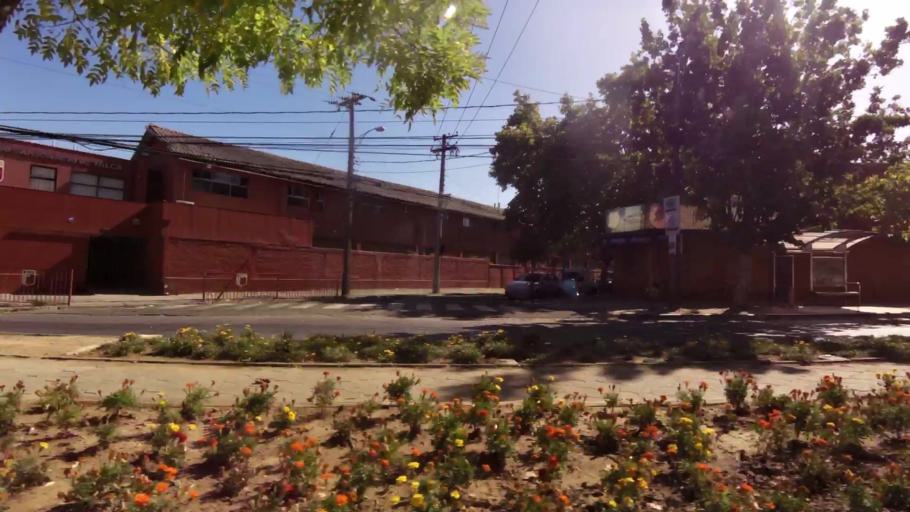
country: CL
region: Maule
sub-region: Provincia de Talca
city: Talca
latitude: -35.4230
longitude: -71.6693
